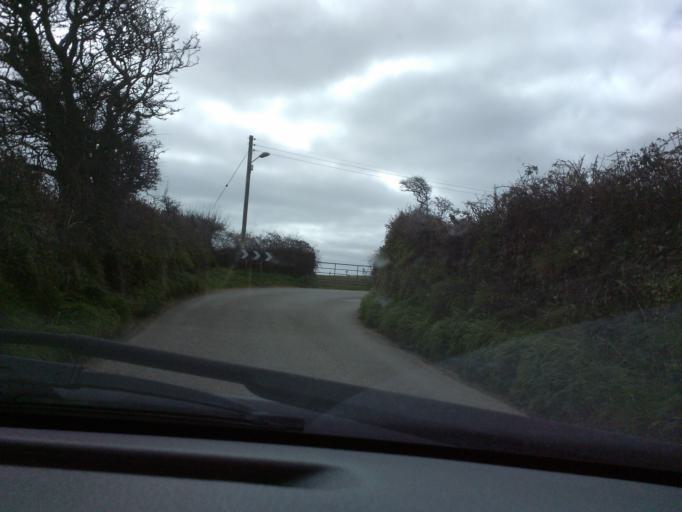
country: GB
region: England
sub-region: Cornwall
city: Penzance
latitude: 50.0864
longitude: -5.5520
